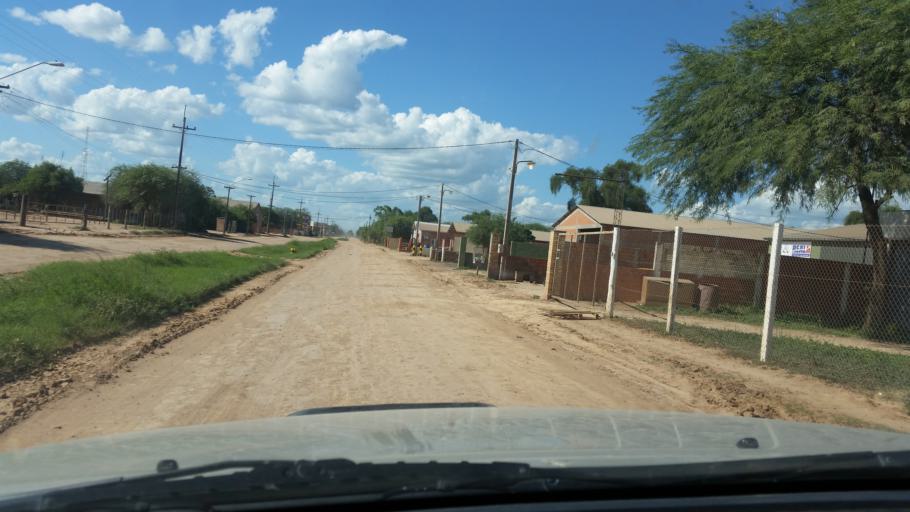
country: PY
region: Boqueron
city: Filadelfia
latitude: -22.3641
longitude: -60.0309
